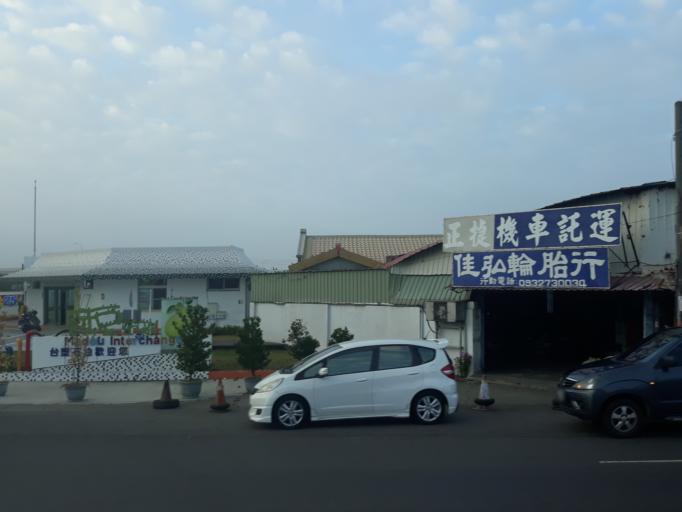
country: TW
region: Taiwan
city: Xinying
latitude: 23.1836
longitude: 120.2381
